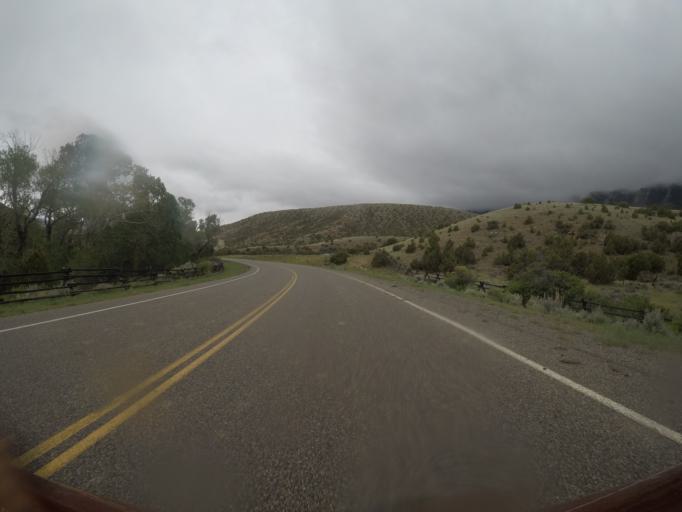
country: US
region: Wyoming
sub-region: Big Horn County
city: Lovell
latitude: 45.0821
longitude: -108.2604
